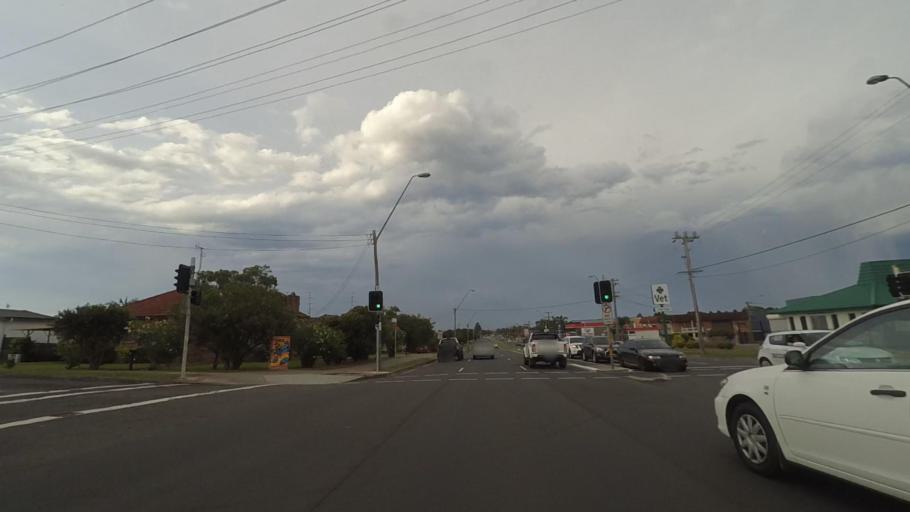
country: AU
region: New South Wales
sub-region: Shellharbour
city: Lake Illawarra
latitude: -34.5464
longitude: 150.8618
